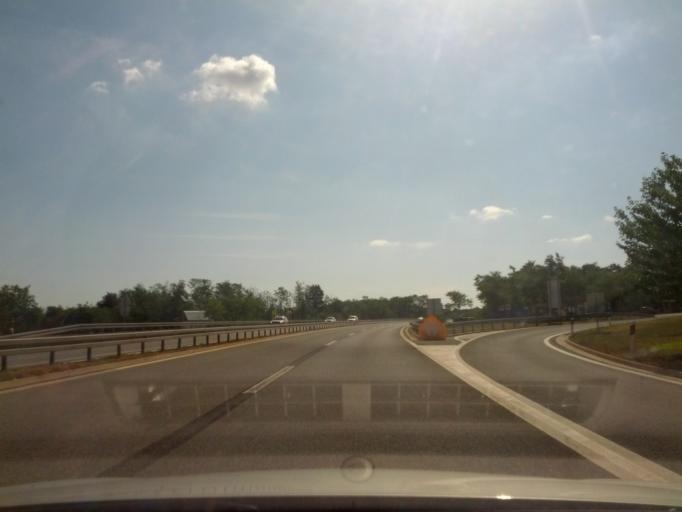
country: HR
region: Istarska
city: Buje
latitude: 45.3201
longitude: 13.6881
